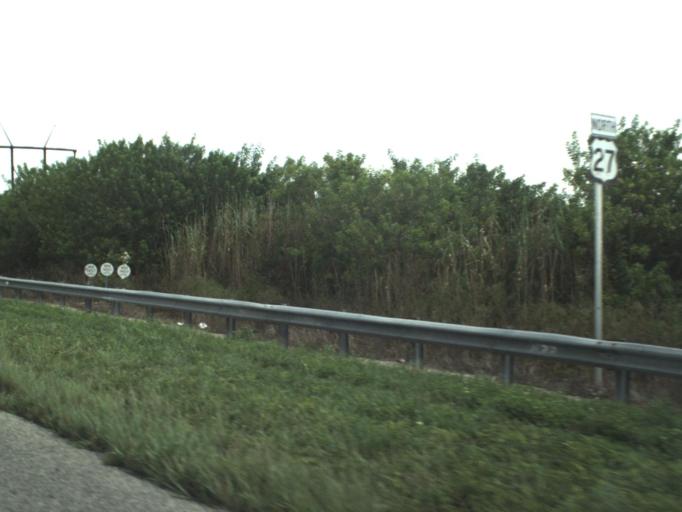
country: US
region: Florida
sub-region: Broward County
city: Weston
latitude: 26.2317
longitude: -80.4607
